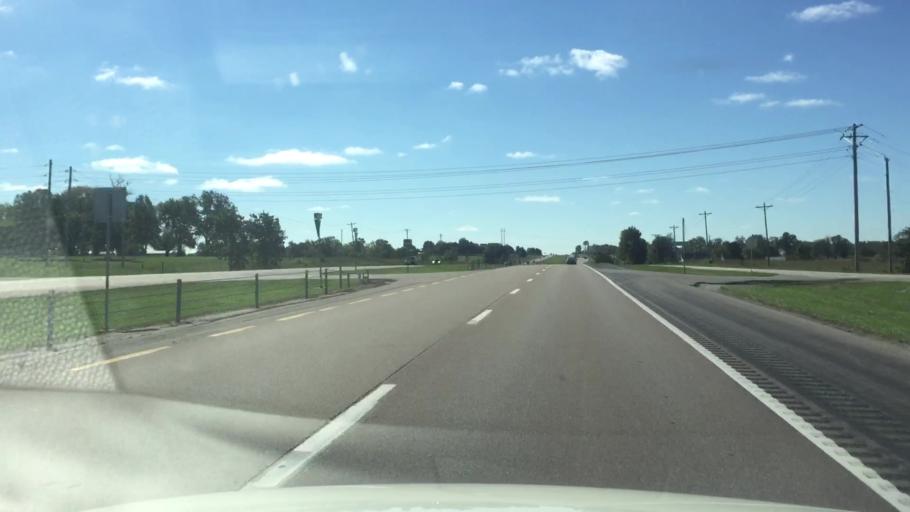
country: US
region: Missouri
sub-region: Boone County
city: Ashland
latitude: 38.7991
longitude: -92.2517
